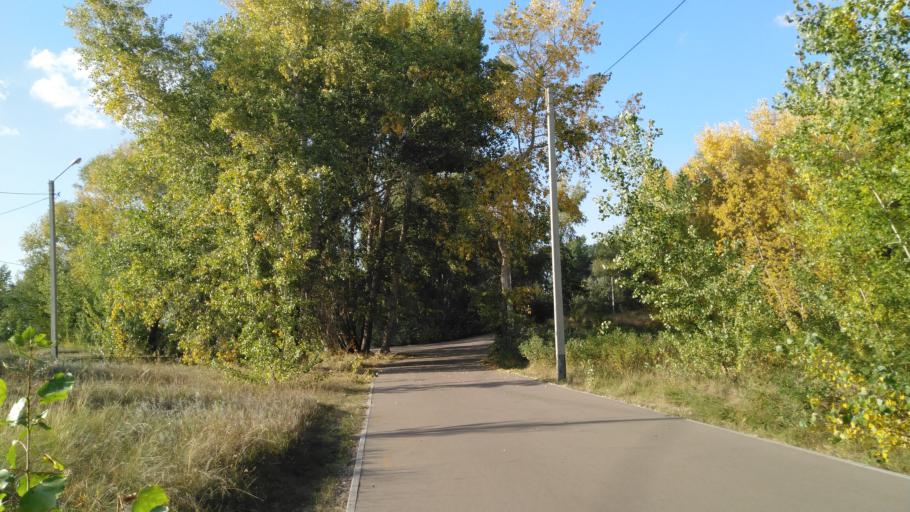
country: KZ
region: Pavlodar
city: Pavlodar
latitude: 52.2624
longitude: 76.9314
